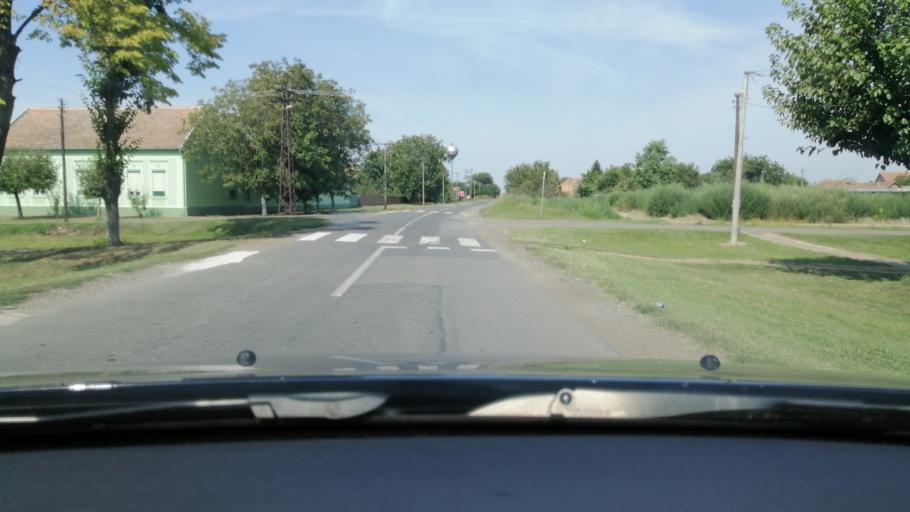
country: RS
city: Orlovat
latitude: 45.2481
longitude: 20.5837
